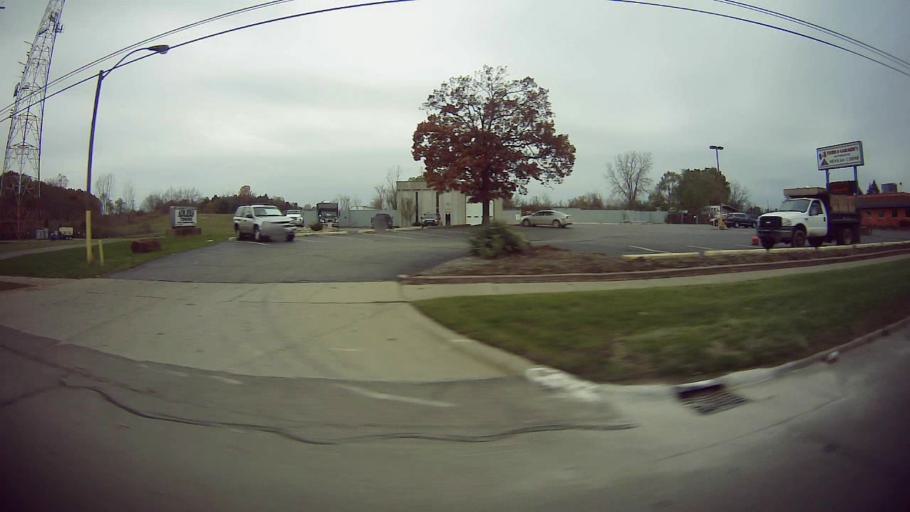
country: US
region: Michigan
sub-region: Oakland County
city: Pontiac
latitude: 42.6650
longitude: -83.3318
